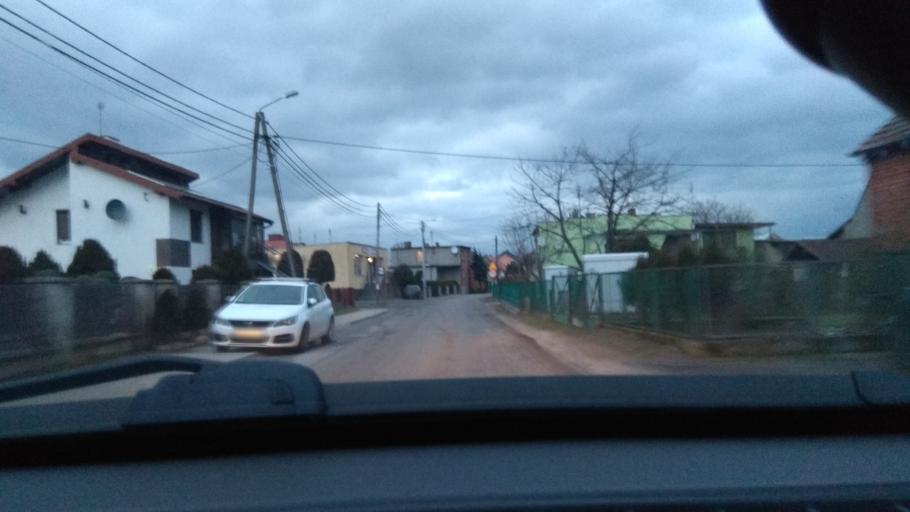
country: PL
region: Greater Poland Voivodeship
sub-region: Powiat kepinski
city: Slupia pod Kepnem
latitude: 51.3019
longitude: 18.0791
